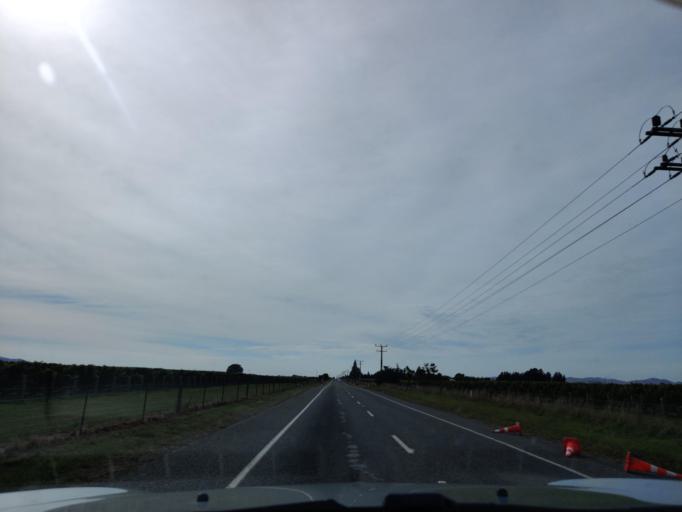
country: NZ
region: Marlborough
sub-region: Marlborough District
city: Blenheim
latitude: -41.5158
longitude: 173.7867
